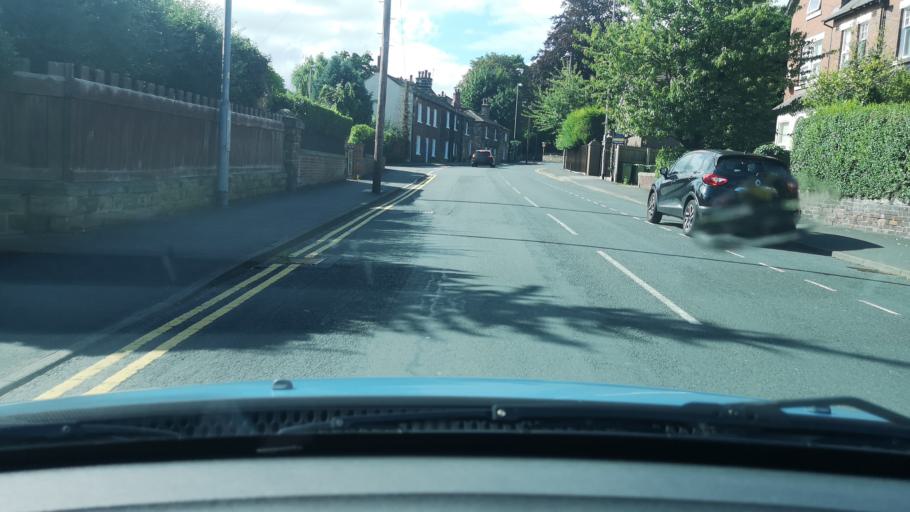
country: GB
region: England
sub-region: City and Borough of Wakefield
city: Walton
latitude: 53.6627
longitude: -1.4831
